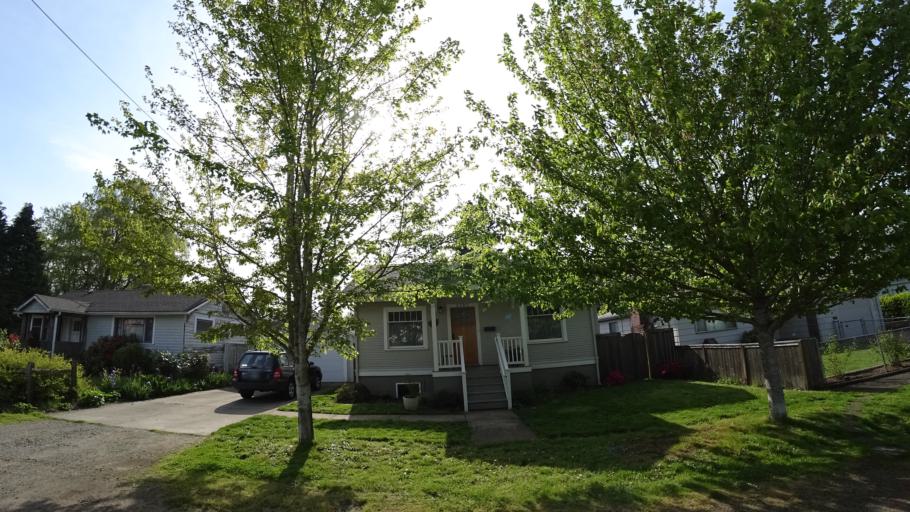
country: US
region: Oregon
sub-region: Clackamas County
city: Milwaukie
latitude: 45.4758
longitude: -122.6135
